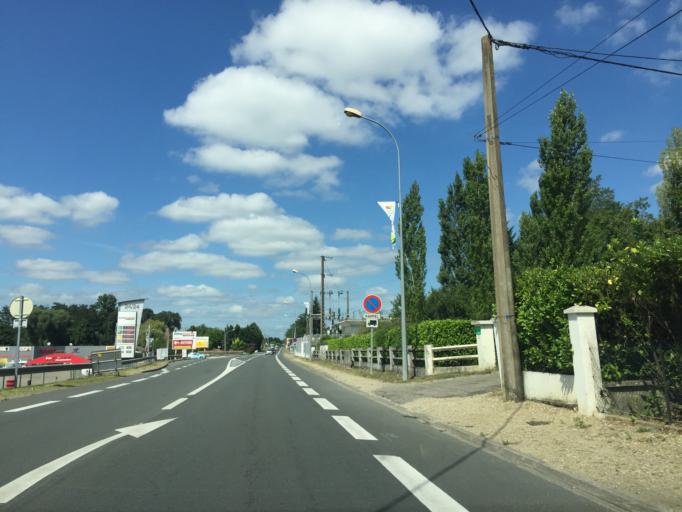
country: FR
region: Aquitaine
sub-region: Departement du Lot-et-Garonne
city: Casteljaloux
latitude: 44.3182
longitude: 0.0939
